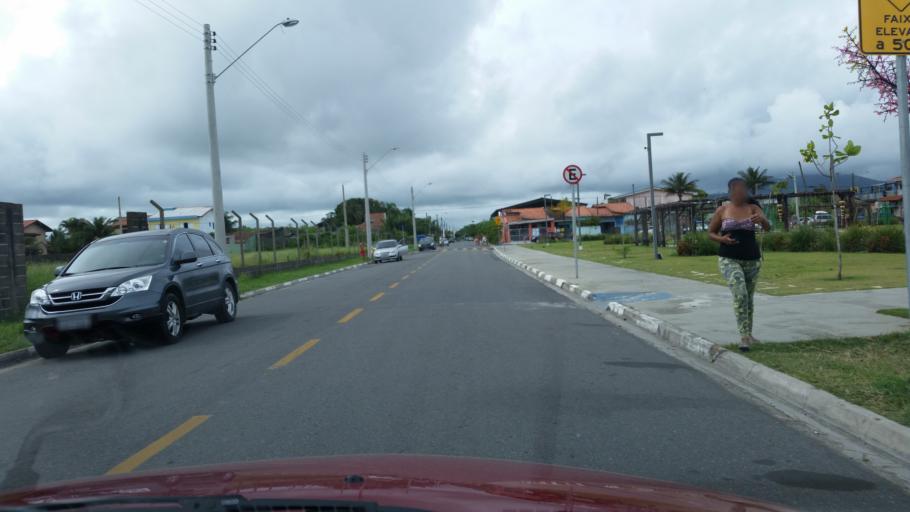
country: BR
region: Sao Paulo
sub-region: Iguape
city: Iguape
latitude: -24.7468
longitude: -47.5539
